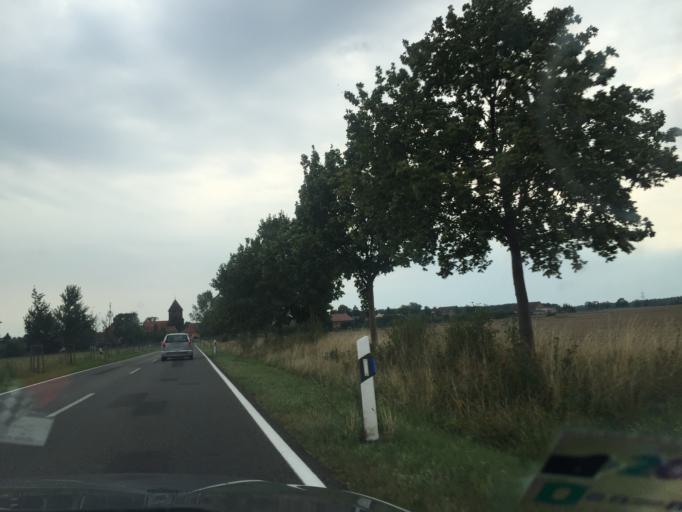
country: DE
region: Brandenburg
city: Wandlitz
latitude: 52.7589
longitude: 13.3777
